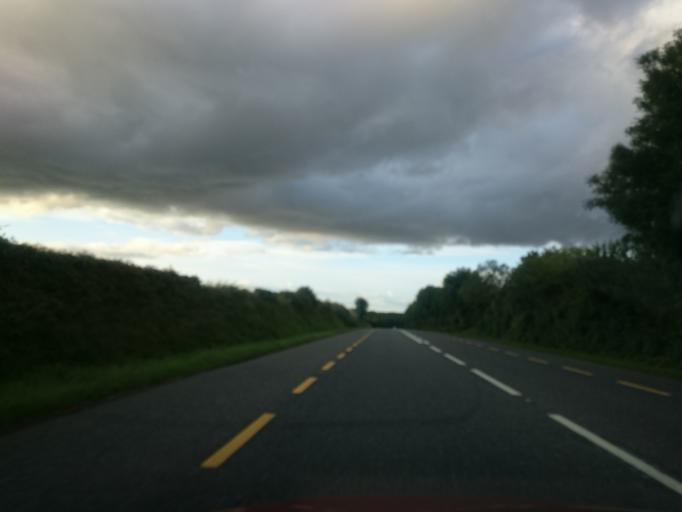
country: IE
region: Leinster
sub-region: Loch Garman
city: Ferns
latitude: 52.5672
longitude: -6.5247
